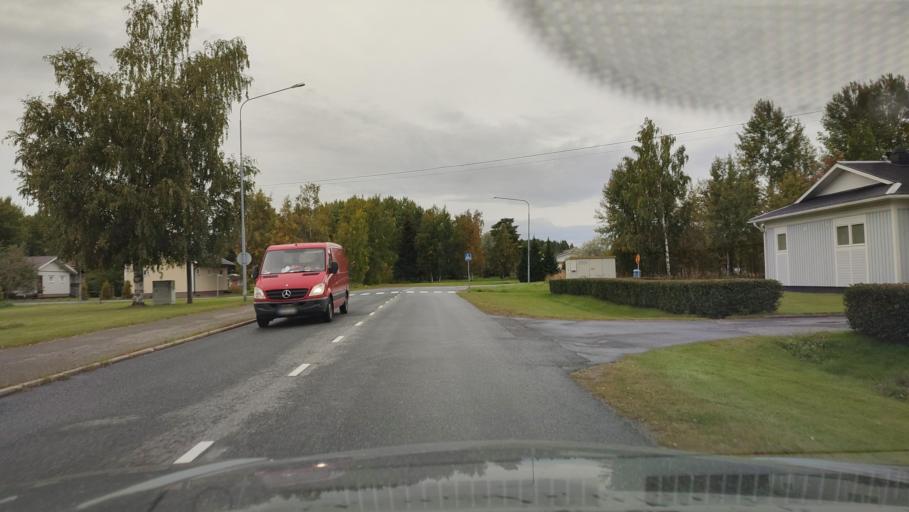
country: FI
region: Ostrobothnia
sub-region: Sydosterbotten
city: Kristinestad
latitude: 62.2812
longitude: 21.3637
